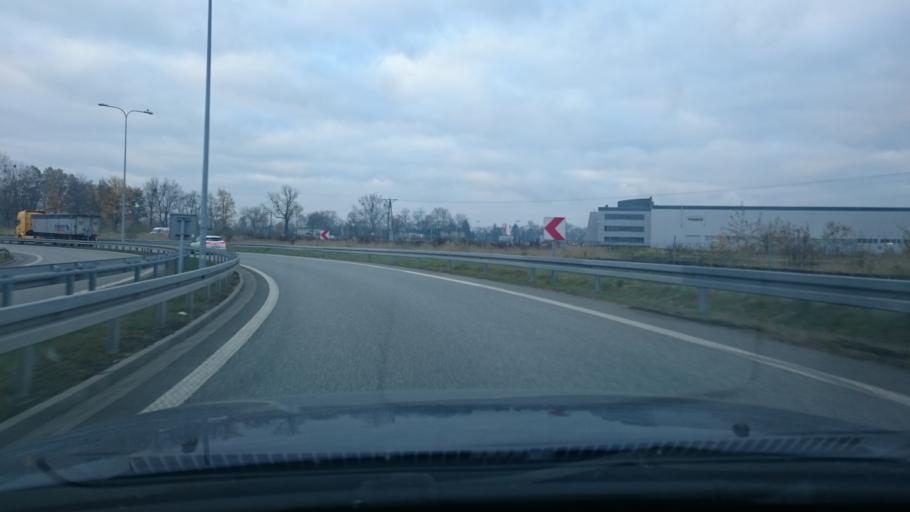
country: PL
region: Silesian Voivodeship
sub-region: Powiat rybnicki
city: Stanowice
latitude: 50.1322
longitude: 18.6836
